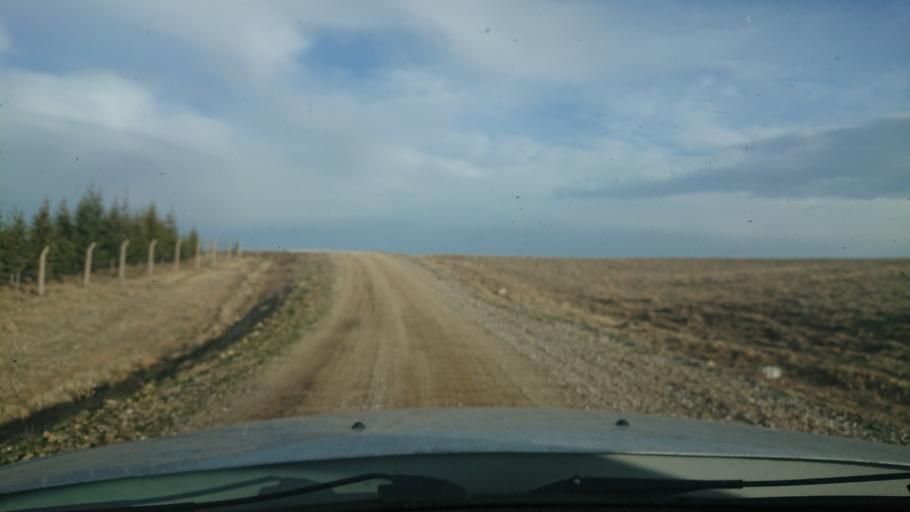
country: TR
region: Aksaray
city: Agacoren
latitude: 38.7153
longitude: 33.8691
